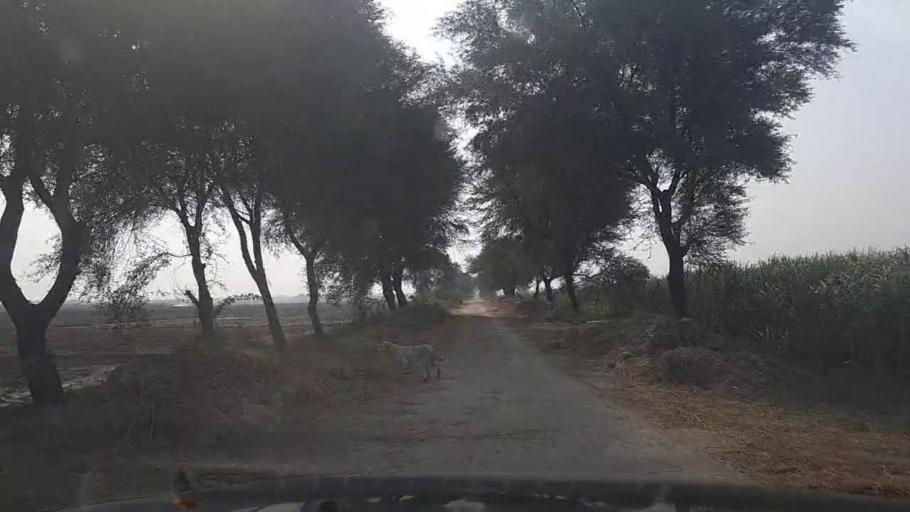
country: PK
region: Sindh
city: Bulri
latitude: 25.0224
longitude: 68.2992
